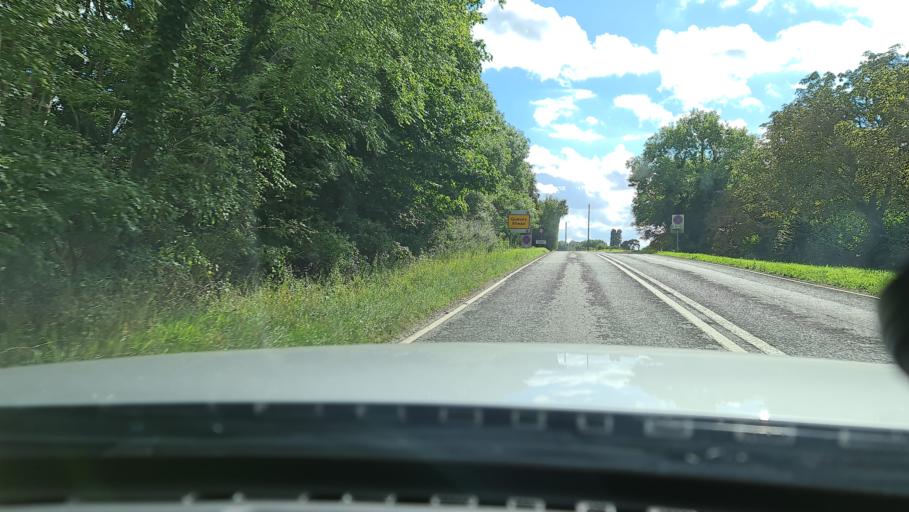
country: GB
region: England
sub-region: Oxfordshire
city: Somerton
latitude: 51.9127
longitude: -1.2256
